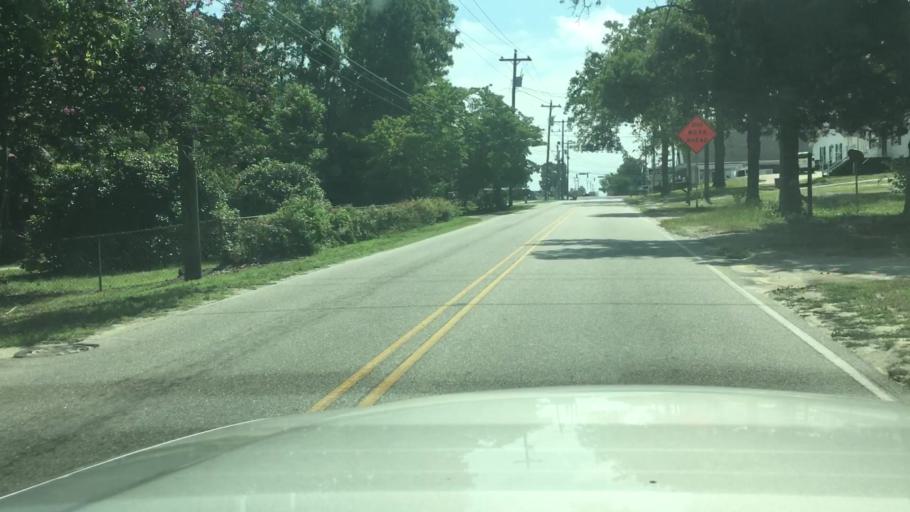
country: US
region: North Carolina
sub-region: Cumberland County
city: Fayetteville
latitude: 35.0136
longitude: -78.8999
